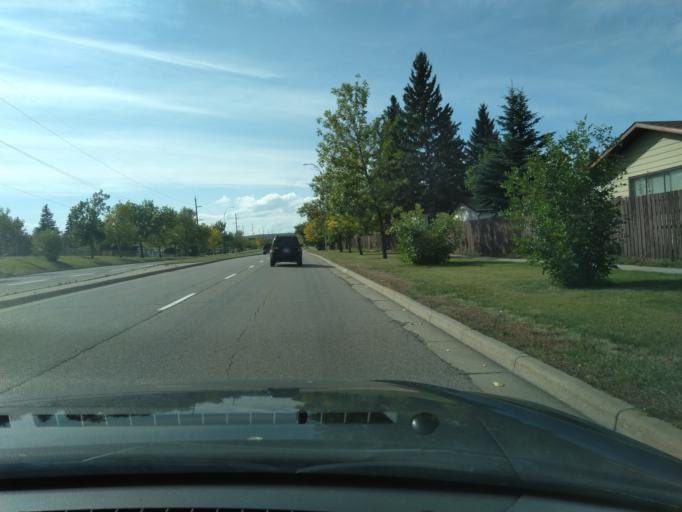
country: CA
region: Alberta
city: Calgary
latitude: 51.1252
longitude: -114.0637
